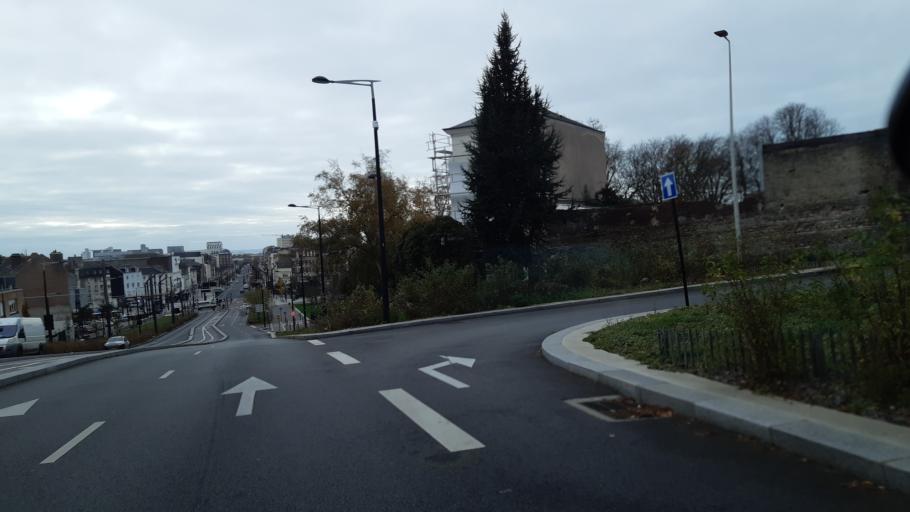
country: FR
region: Haute-Normandie
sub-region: Departement de la Seine-Maritime
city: Le Havre
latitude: 49.5020
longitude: 0.1313
